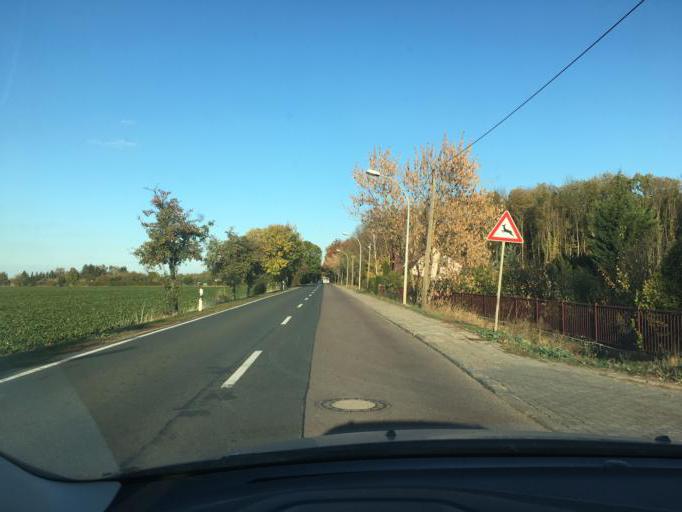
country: DE
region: Saxony-Anhalt
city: Lutzen
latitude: 51.2639
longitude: 12.1496
